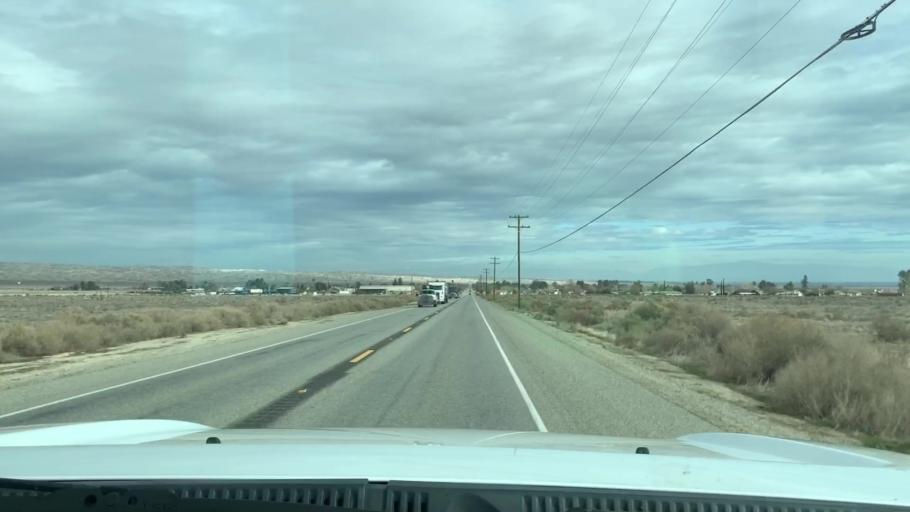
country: US
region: California
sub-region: Kern County
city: Ford City
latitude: 35.2010
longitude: -119.4182
